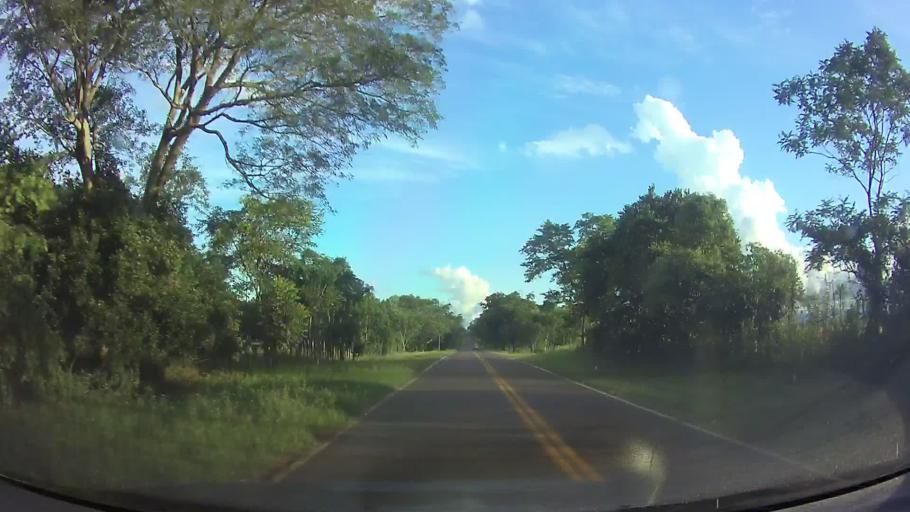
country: PY
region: Paraguari
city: Acahay
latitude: -25.9395
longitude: -57.0988
